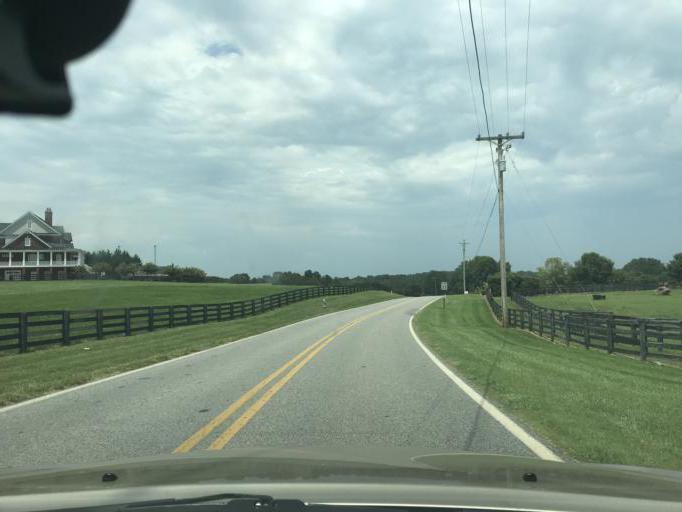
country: US
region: Georgia
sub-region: Forsyth County
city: Cumming
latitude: 34.2804
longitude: -84.2146
